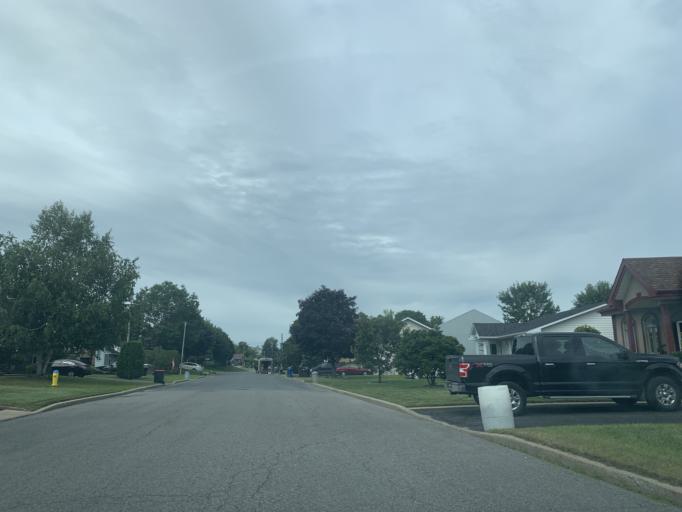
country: CA
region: Ontario
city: Hawkesbury
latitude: 45.5992
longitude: -74.6005
